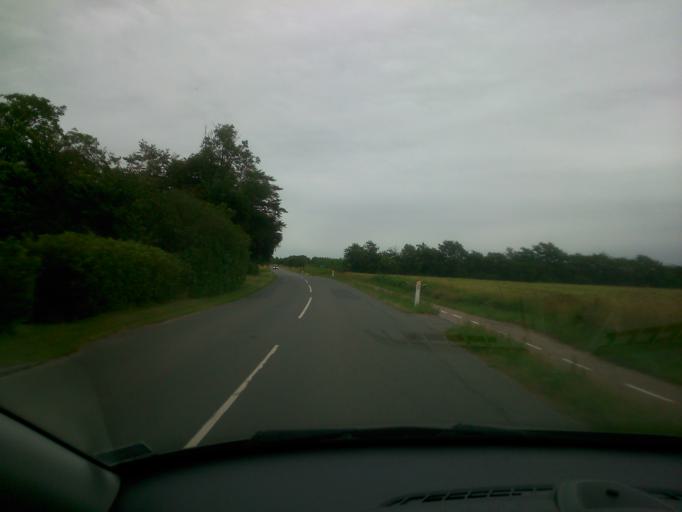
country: DK
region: Central Jutland
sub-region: Ringkobing-Skjern Kommune
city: Skjern
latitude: 55.9501
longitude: 8.4092
